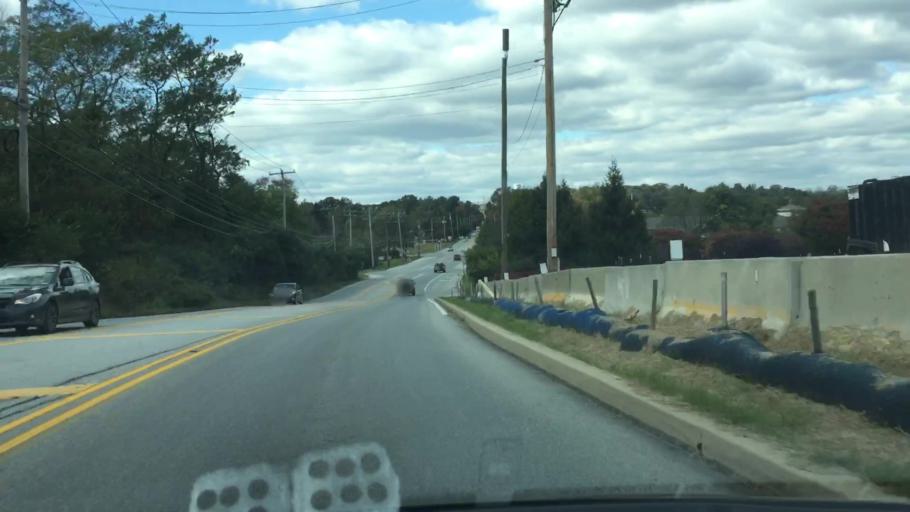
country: US
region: Pennsylvania
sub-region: Chester County
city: West Chester
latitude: 39.9985
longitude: -75.5712
